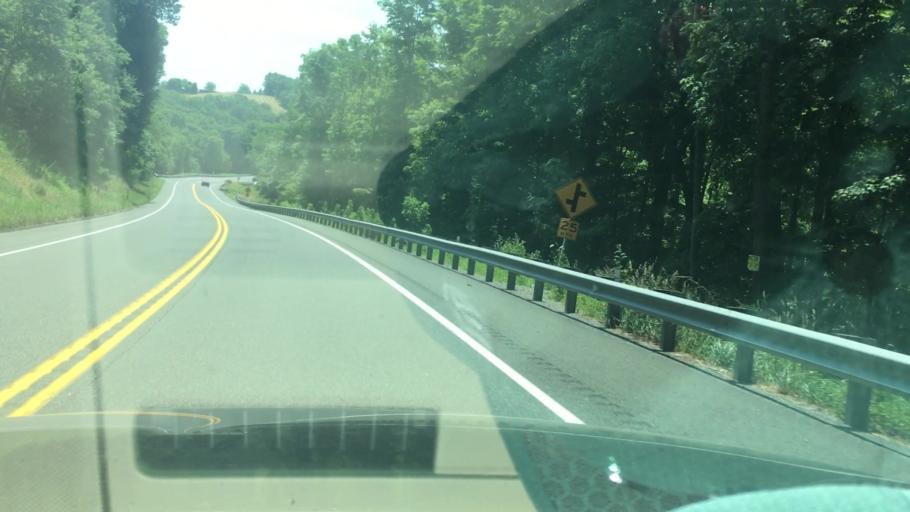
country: US
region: Pennsylvania
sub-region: Lehigh County
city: Schnecksville
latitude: 40.6600
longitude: -75.6864
